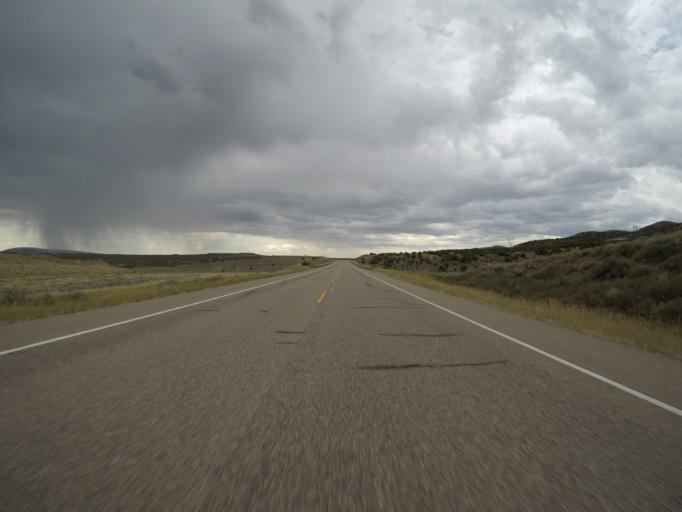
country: US
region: Colorado
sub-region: Rio Blanco County
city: Rangely
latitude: 40.3622
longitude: -108.4251
